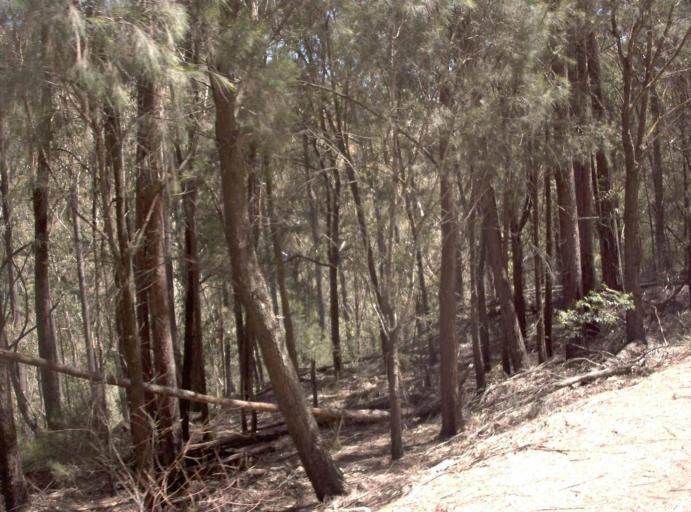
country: AU
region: Victoria
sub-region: East Gippsland
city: Lakes Entrance
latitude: -37.3744
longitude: 148.2180
